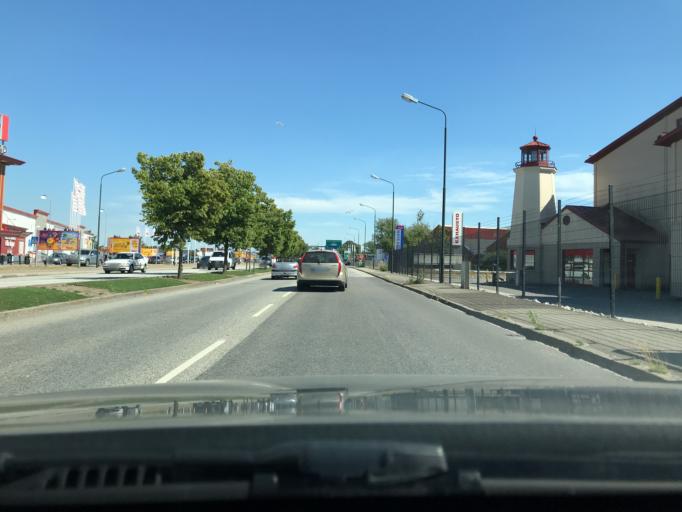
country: SE
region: Skane
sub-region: Malmo
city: Malmoe
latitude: 55.5731
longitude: 13.0350
